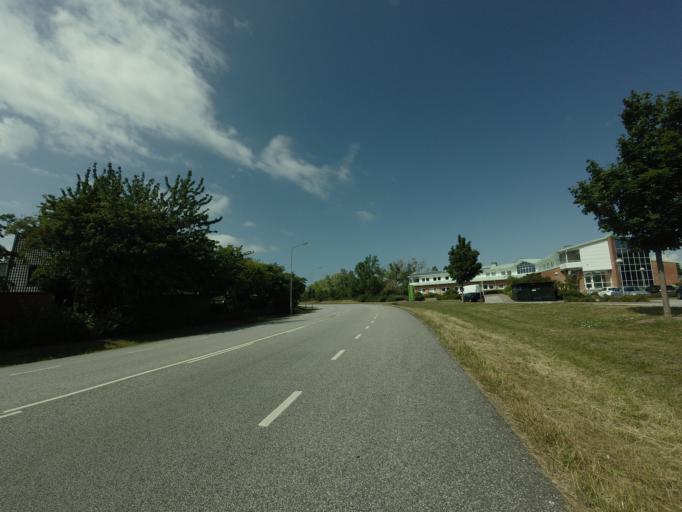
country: SE
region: Skane
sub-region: Malmo
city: Malmoe
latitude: 55.5649
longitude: 12.9944
